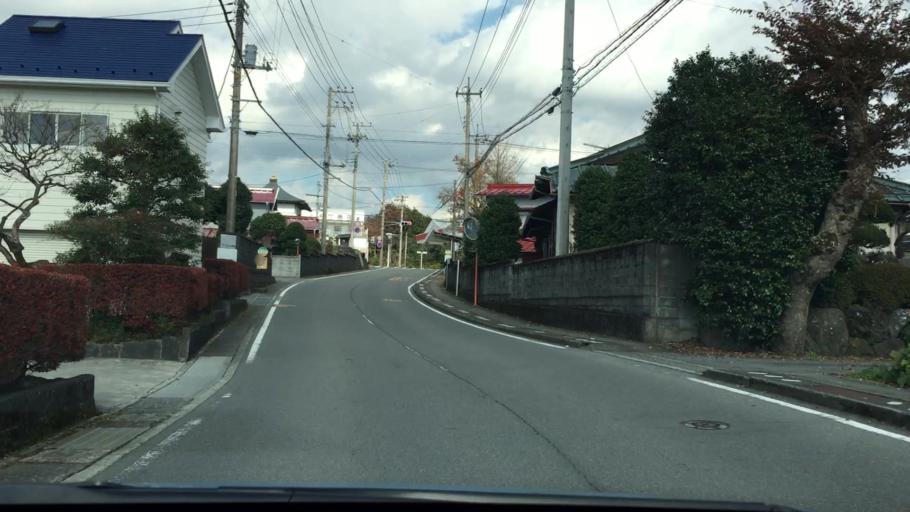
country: JP
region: Shizuoka
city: Gotemba
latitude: 35.3492
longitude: 138.9447
